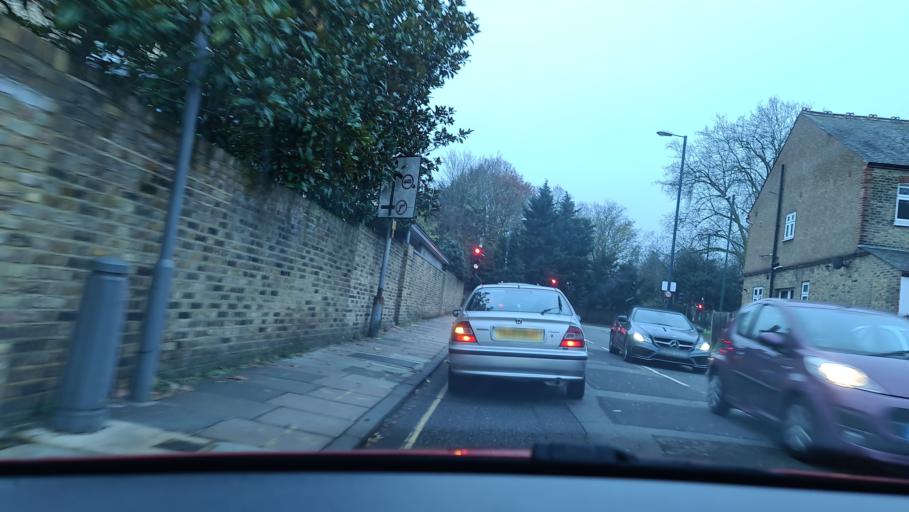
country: GB
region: England
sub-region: Greater London
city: Richmond
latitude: 51.4623
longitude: -0.2882
